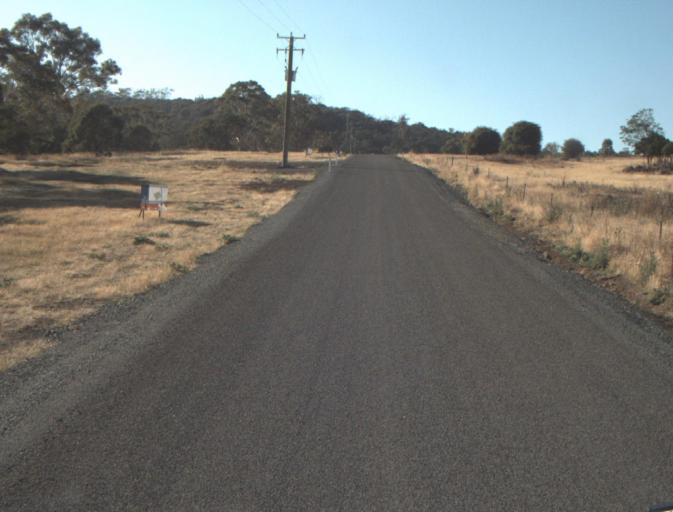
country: AU
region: Tasmania
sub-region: Launceston
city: Newstead
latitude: -41.4353
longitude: 147.2156
